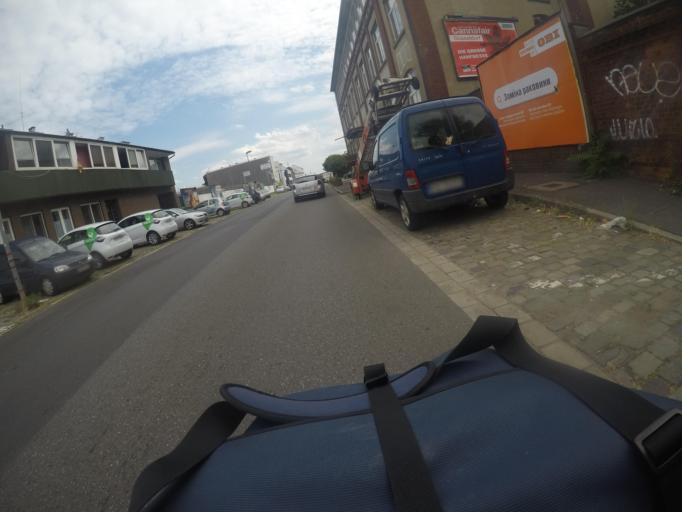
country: DE
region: North Rhine-Westphalia
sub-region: Regierungsbezirk Dusseldorf
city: Dusseldorf
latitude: 51.2214
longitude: 6.8257
